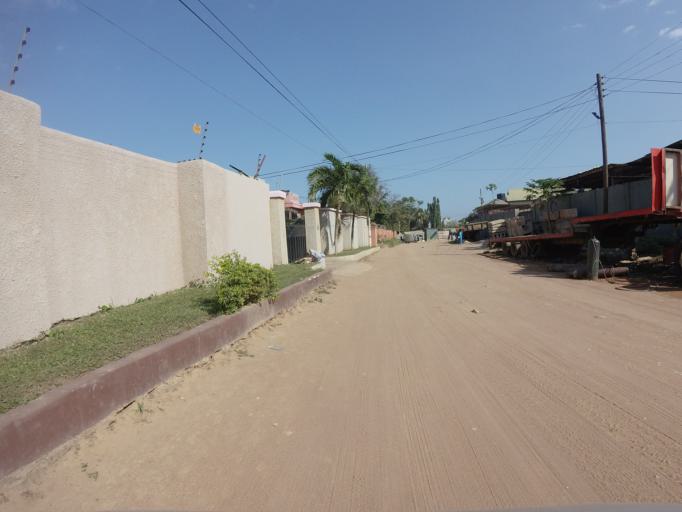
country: GH
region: Greater Accra
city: Dome
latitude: 5.6382
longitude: -0.2370
